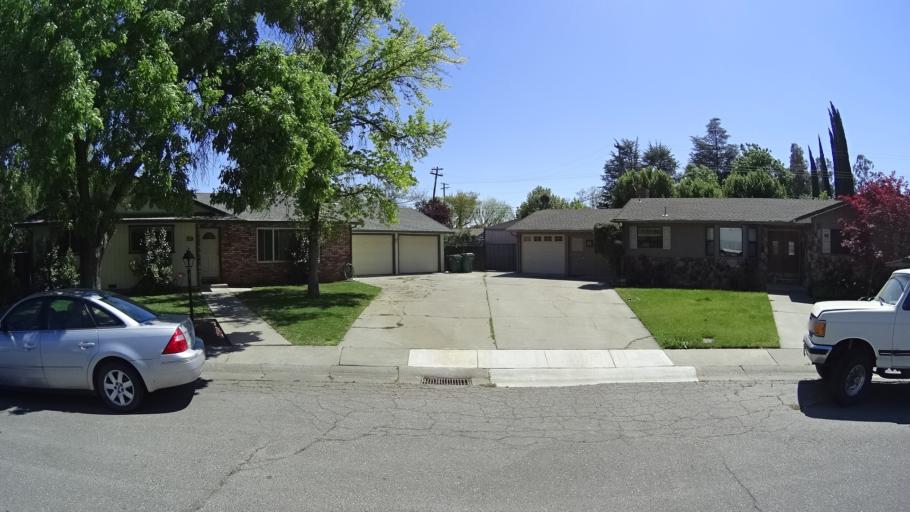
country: US
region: California
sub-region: Glenn County
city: Orland
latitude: 39.7408
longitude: -122.1904
